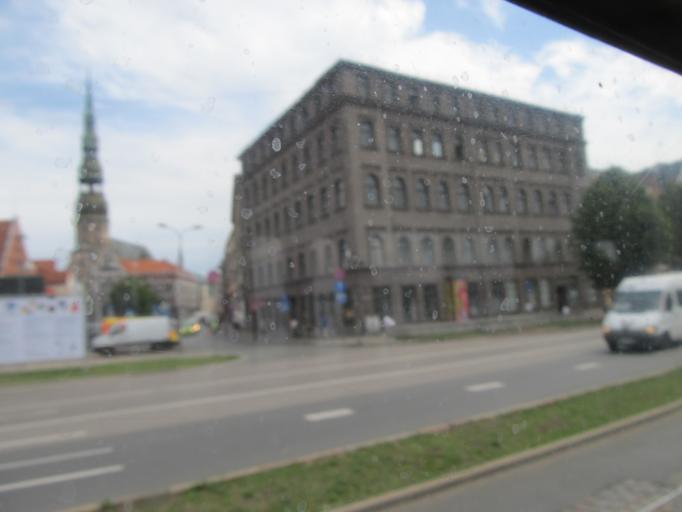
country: LV
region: Riga
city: Riga
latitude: 56.9463
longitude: 24.1049
